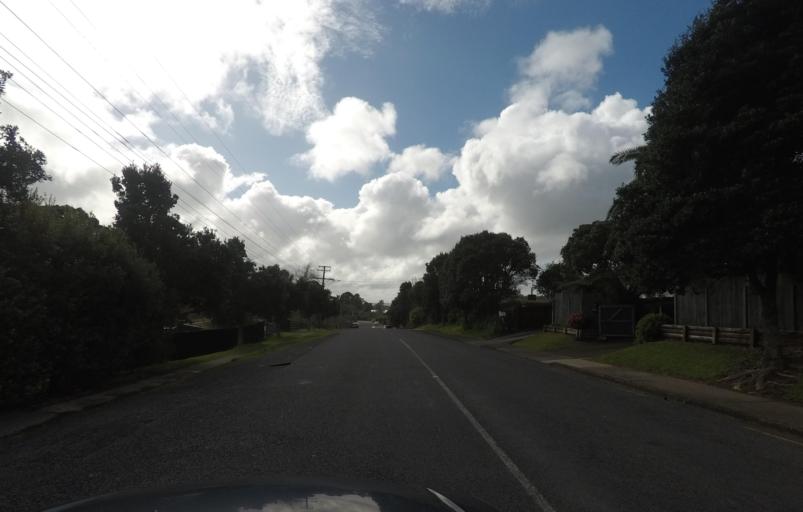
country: NZ
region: Auckland
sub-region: Auckland
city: Muriwai Beach
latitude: -36.8507
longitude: 174.5440
